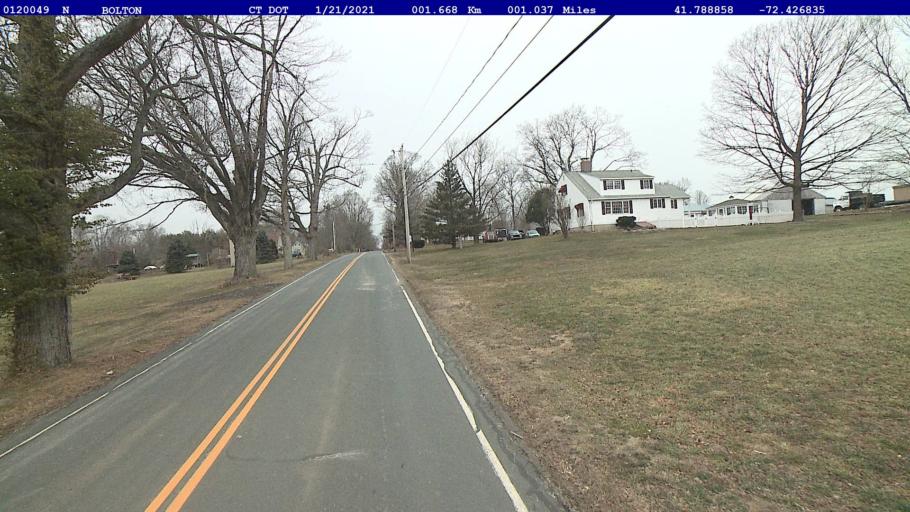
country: US
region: Connecticut
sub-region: Tolland County
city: Rockville
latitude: 41.7889
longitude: -72.4268
